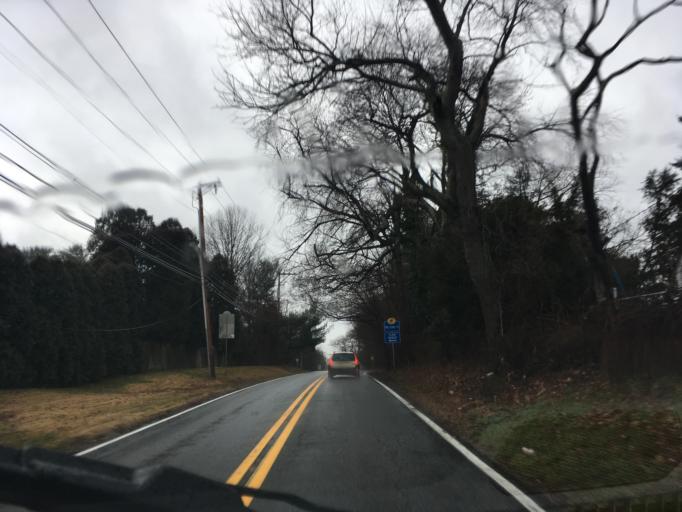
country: US
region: Delaware
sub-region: New Castle County
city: Claymont
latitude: 39.8144
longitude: -75.4992
